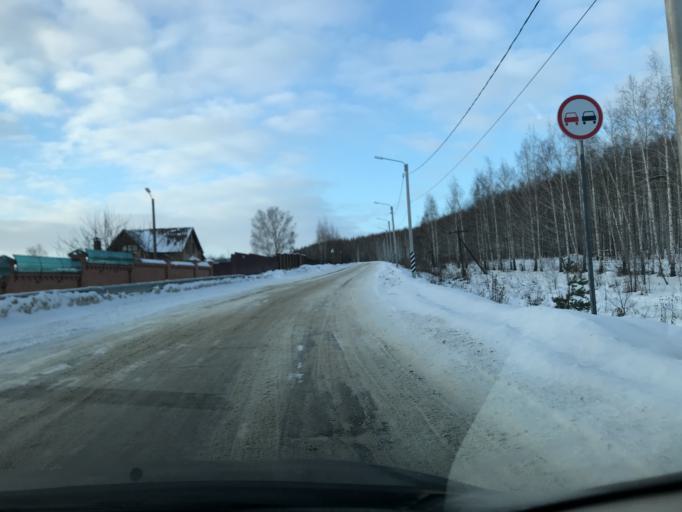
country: RU
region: Ulyanovsk
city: Undory
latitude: 54.6005
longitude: 48.4247
